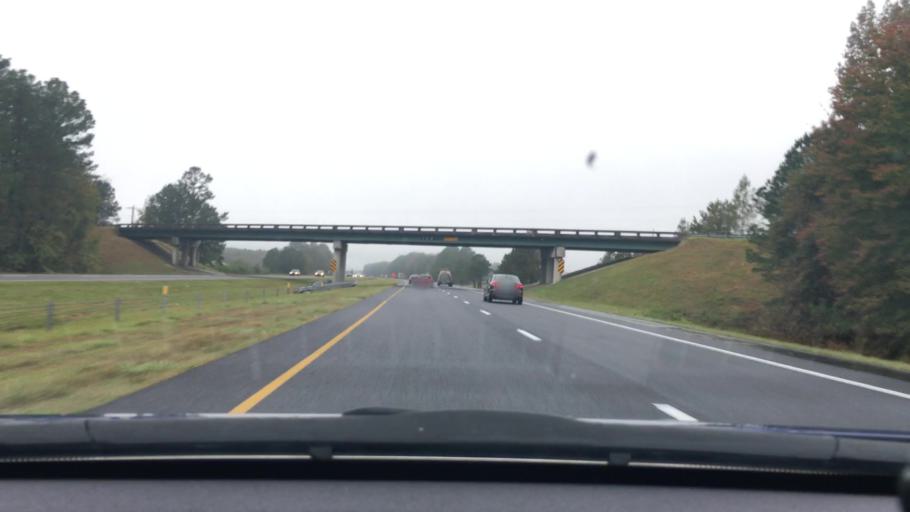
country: US
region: South Carolina
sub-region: Lee County
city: Bishopville
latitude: 34.1943
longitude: -80.1388
